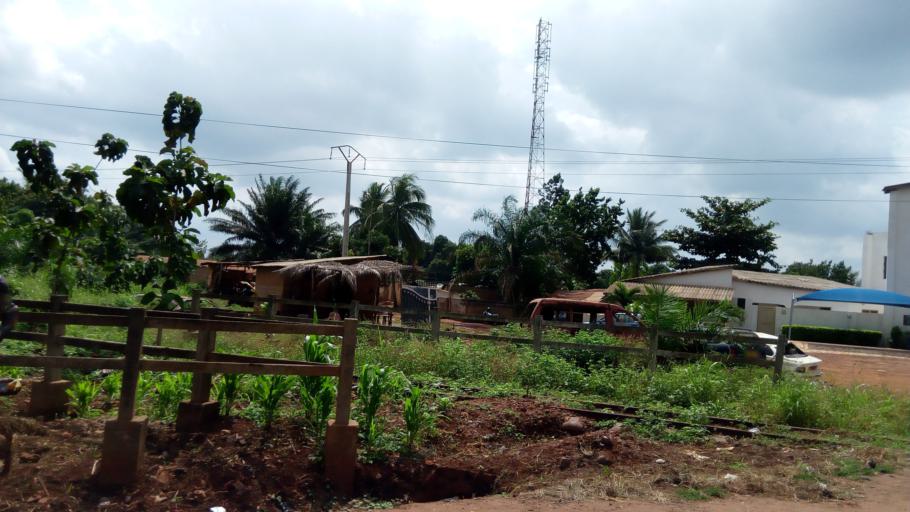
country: TG
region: Maritime
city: Tsevie
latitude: 6.4359
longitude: 1.2115
